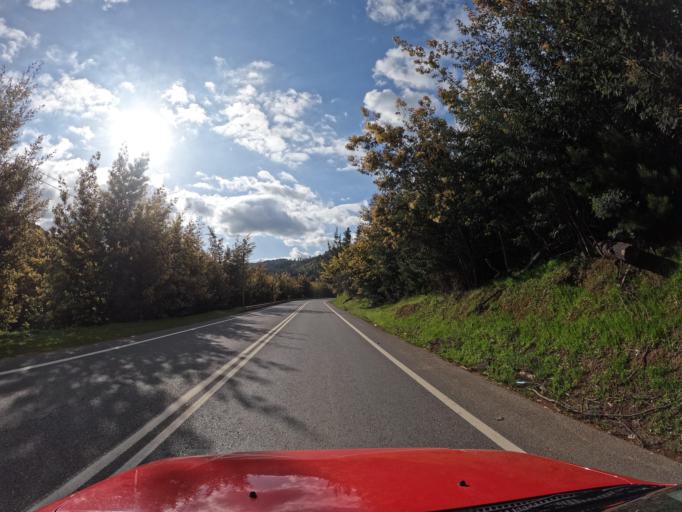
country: CL
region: Maule
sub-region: Provincia de Talca
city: Constitucion
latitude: -35.5411
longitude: -72.1553
